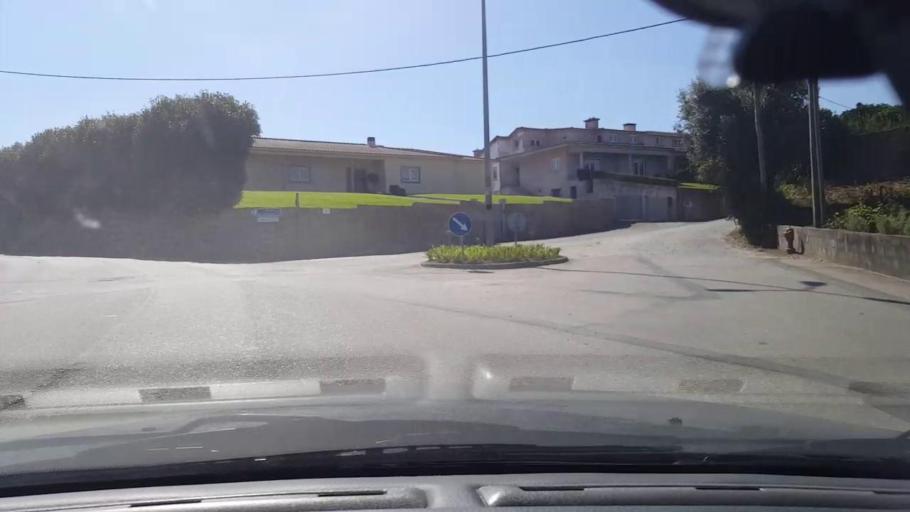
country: PT
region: Porto
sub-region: Matosinhos
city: Lavra
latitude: 41.2670
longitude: -8.6916
